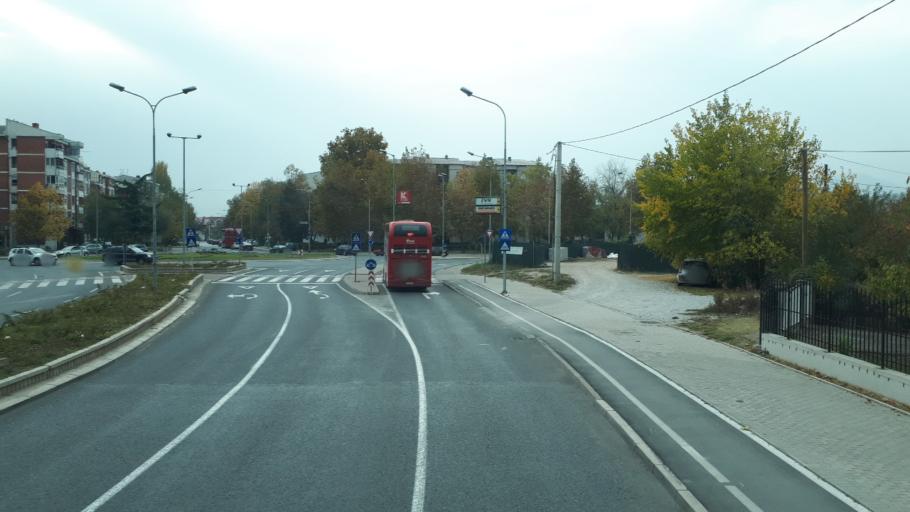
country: MK
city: Krushopek
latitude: 42.0102
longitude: 21.3624
